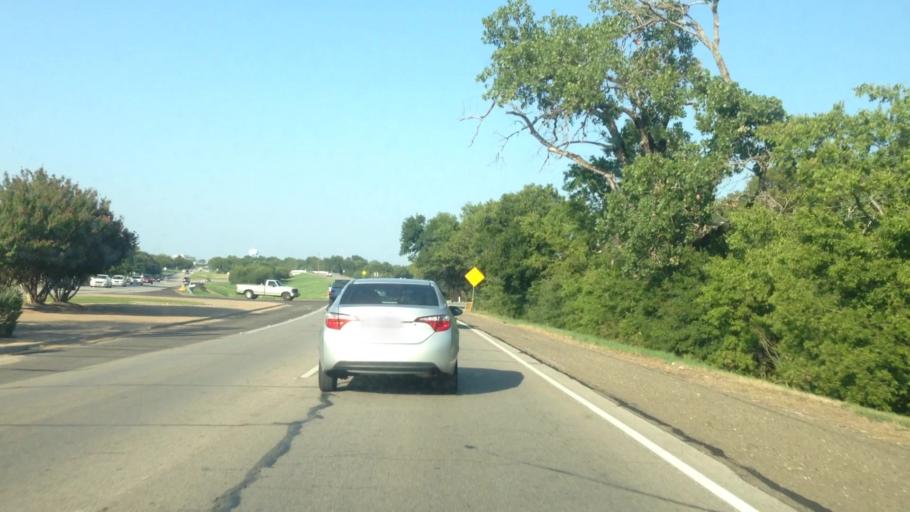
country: US
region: Texas
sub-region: Tarrant County
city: Haltom City
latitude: 32.8066
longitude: -97.2502
